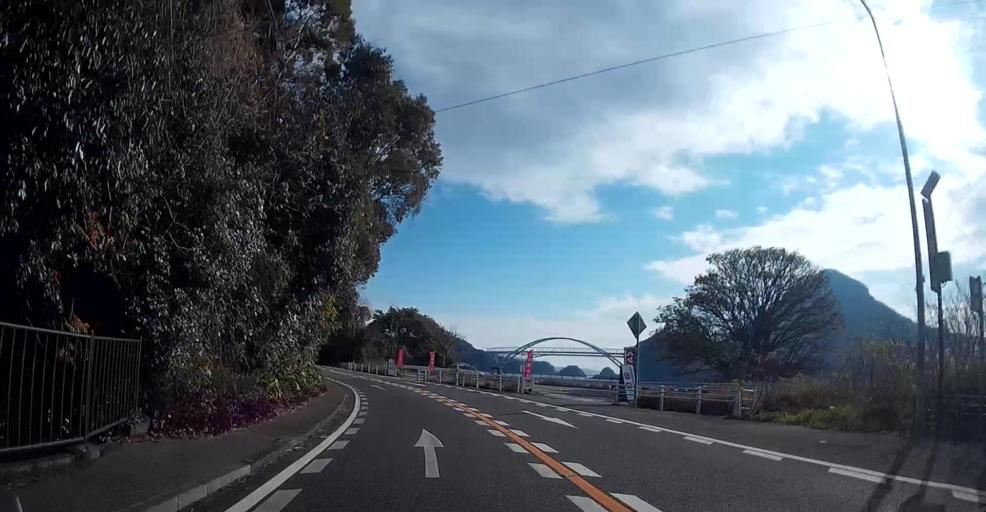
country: JP
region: Kumamoto
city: Yatsushiro
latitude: 32.6214
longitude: 130.4571
